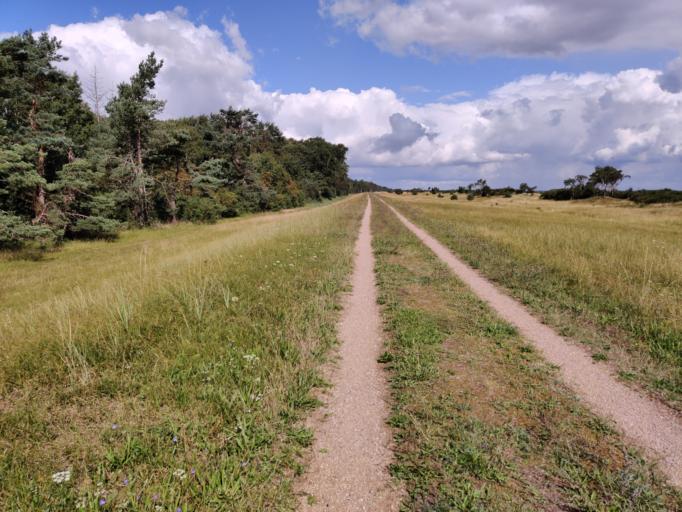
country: DK
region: Zealand
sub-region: Guldborgsund Kommune
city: Nykobing Falster
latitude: 54.6197
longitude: 11.9629
